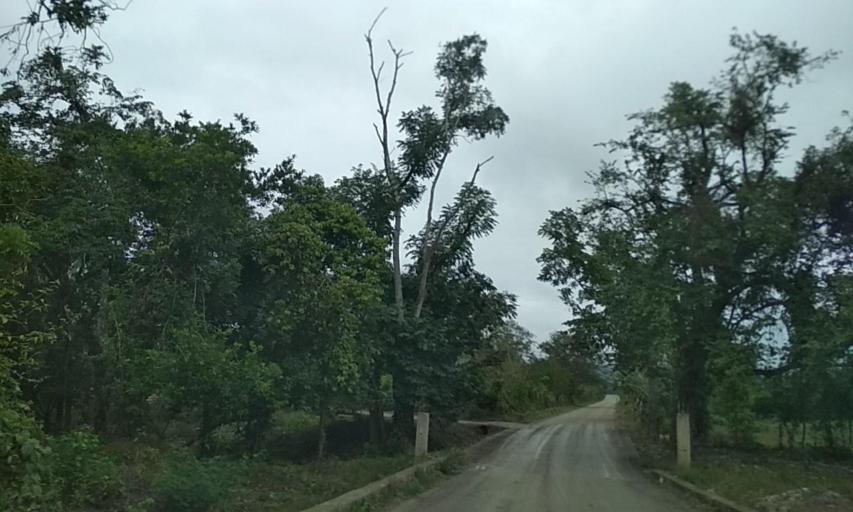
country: MX
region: Veracruz
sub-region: Papantla
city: El Chote
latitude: 20.3862
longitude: -97.3523
